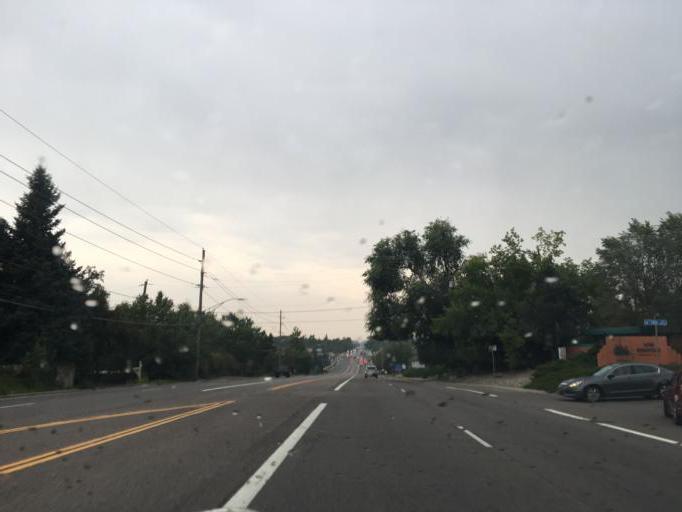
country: US
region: Colorado
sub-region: Jefferson County
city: Wheat Ridge
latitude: 39.7460
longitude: -105.1096
